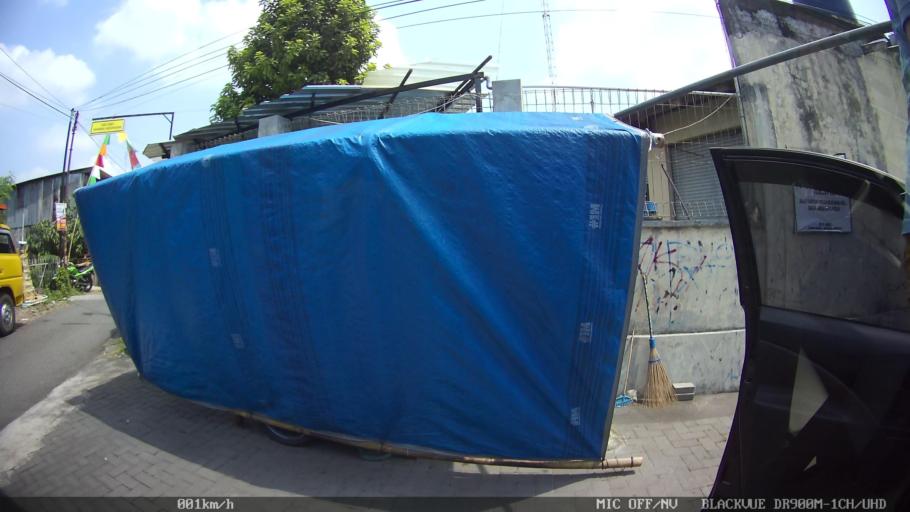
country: ID
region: Daerah Istimewa Yogyakarta
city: Yogyakarta
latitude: -7.8046
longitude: 110.3850
